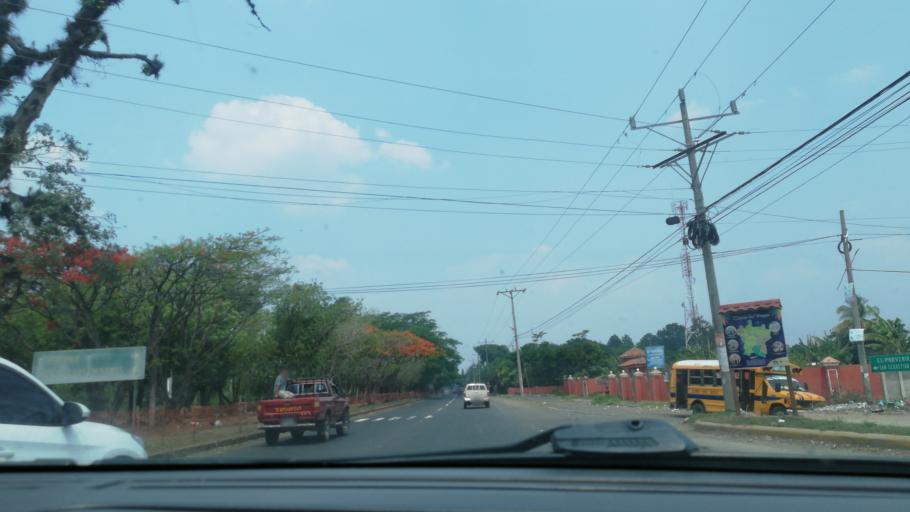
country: SV
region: Santa Ana
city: Chalchuapa
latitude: 13.9878
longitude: -89.6438
